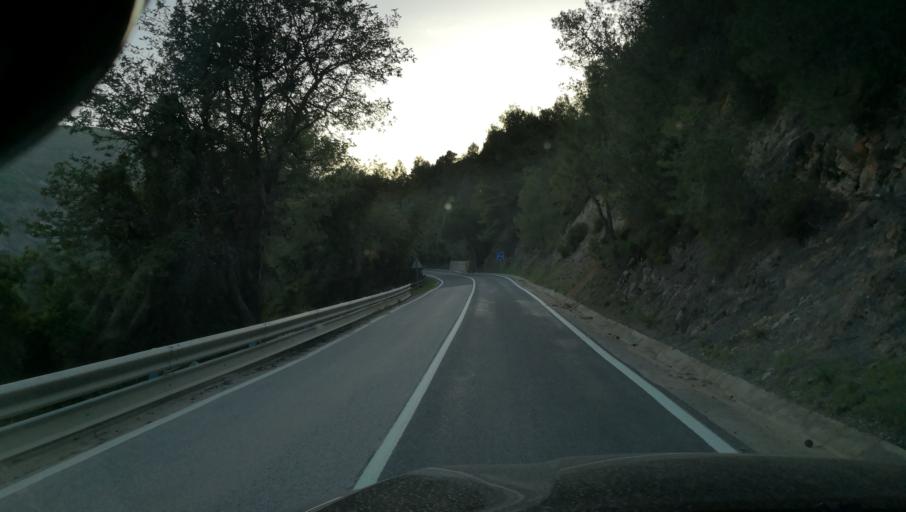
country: PT
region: Setubal
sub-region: Setubal
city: Setubal
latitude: 38.4958
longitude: -8.9374
